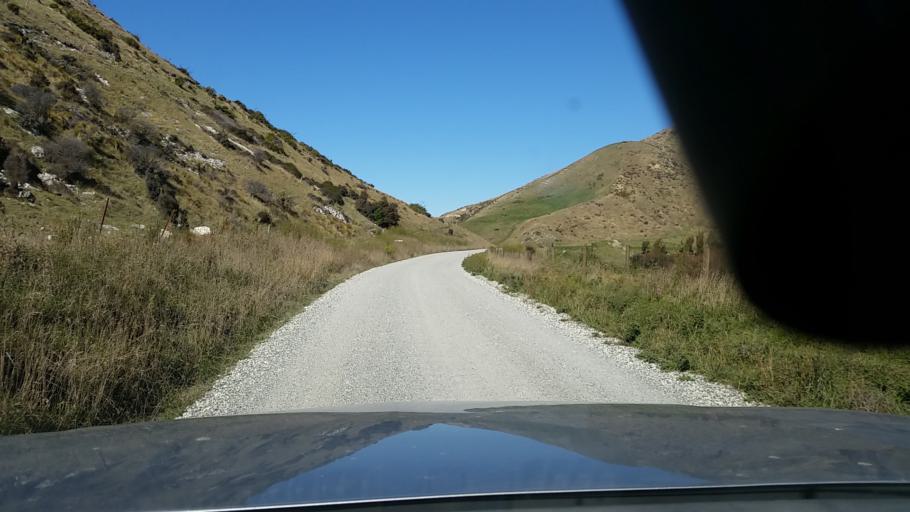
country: NZ
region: Marlborough
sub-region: Marlborough District
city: Blenheim
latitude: -41.8342
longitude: 174.1758
